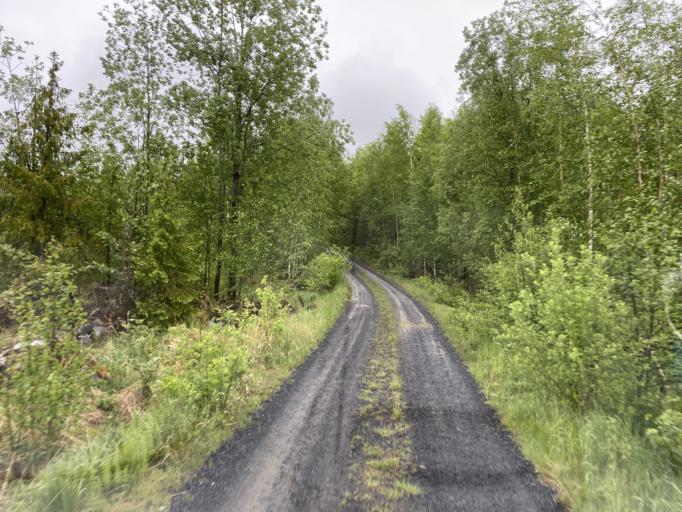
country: FI
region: Pirkanmaa
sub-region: Etelae-Pirkanmaa
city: Urjala
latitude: 60.9542
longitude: 23.5572
